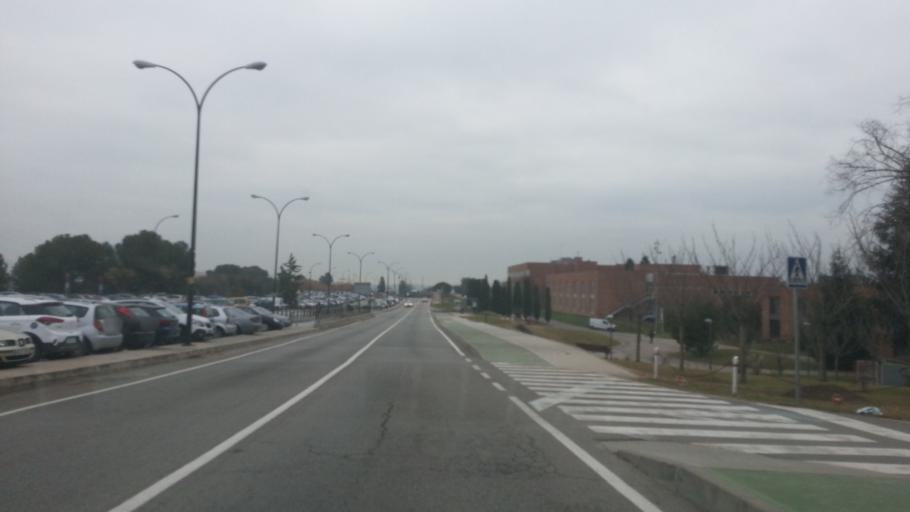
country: ES
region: Catalonia
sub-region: Provincia de Barcelona
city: Barbera del Valles
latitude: 41.5060
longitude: 2.1049
